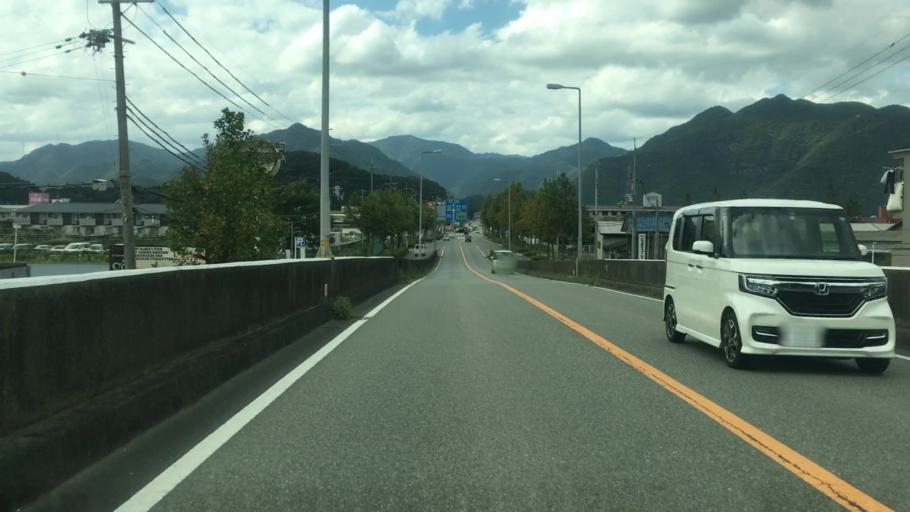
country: JP
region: Kyoto
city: Fukuchiyama
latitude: 35.1524
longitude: 135.0511
